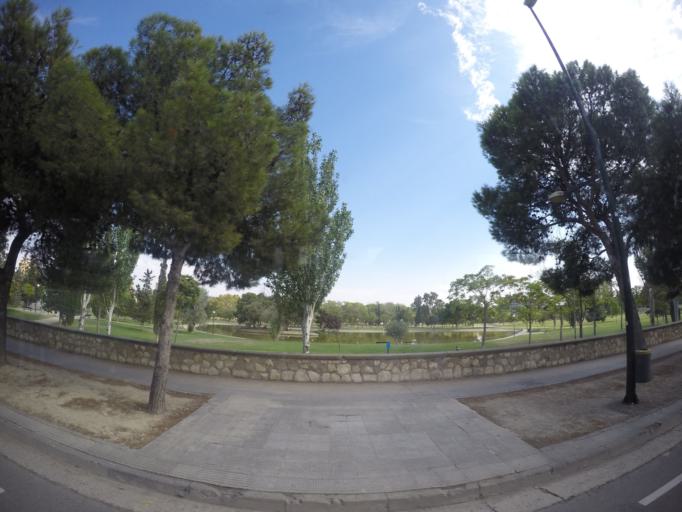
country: ES
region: Aragon
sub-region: Provincia de Zaragoza
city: Zaragoza
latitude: 41.6660
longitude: -0.8794
